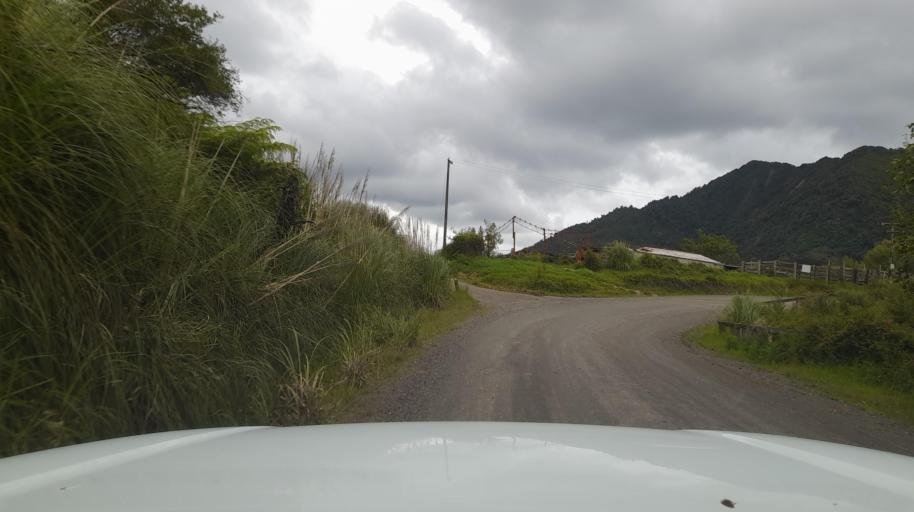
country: NZ
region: Northland
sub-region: Far North District
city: Kaitaia
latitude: -35.3299
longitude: 173.3551
